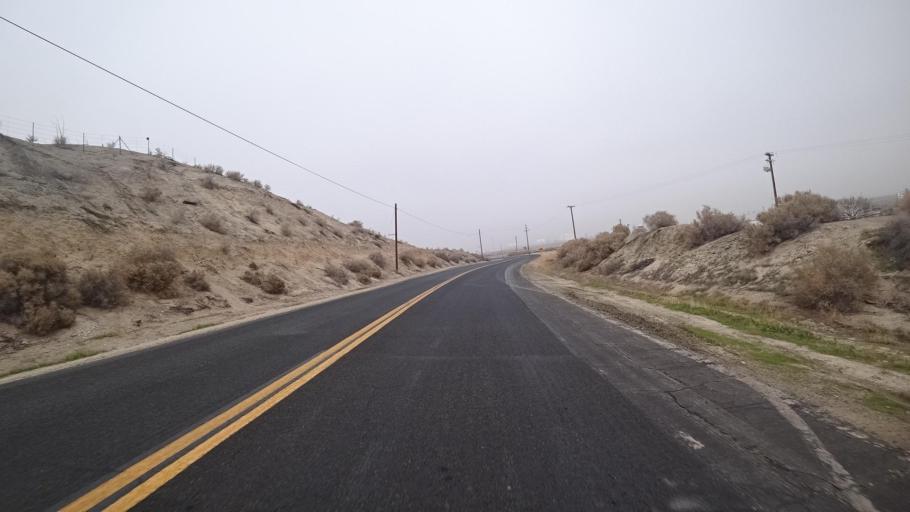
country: US
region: California
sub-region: Kern County
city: Ford City
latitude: 35.2641
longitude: -119.3121
